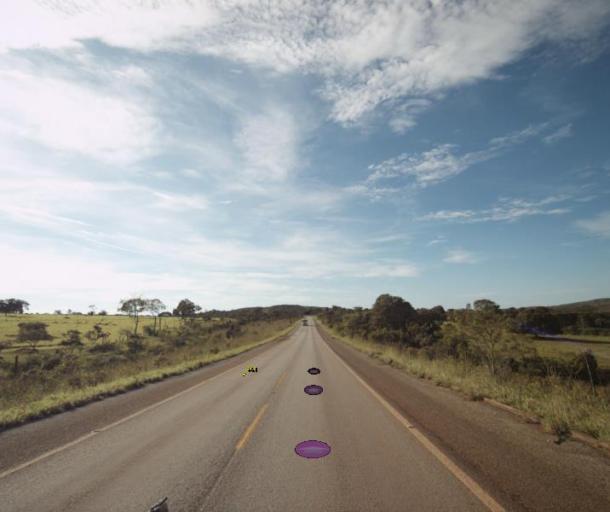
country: BR
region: Goias
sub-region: Pirenopolis
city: Pirenopolis
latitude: -15.7667
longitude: -48.5676
